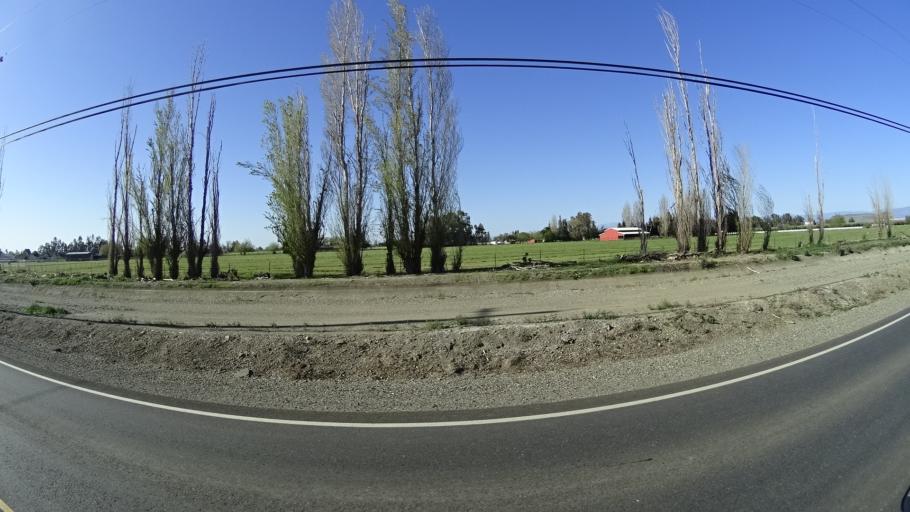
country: US
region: California
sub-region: Glenn County
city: Orland
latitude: 39.7621
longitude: -122.2339
